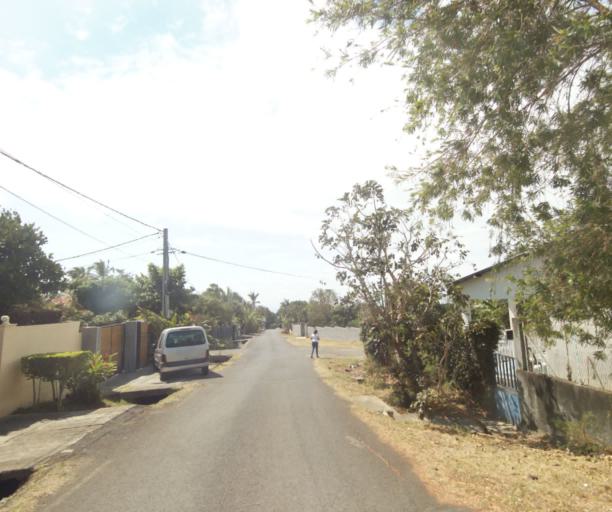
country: RE
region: Reunion
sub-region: Reunion
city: Saint-Paul
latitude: -21.0559
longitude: 55.2588
